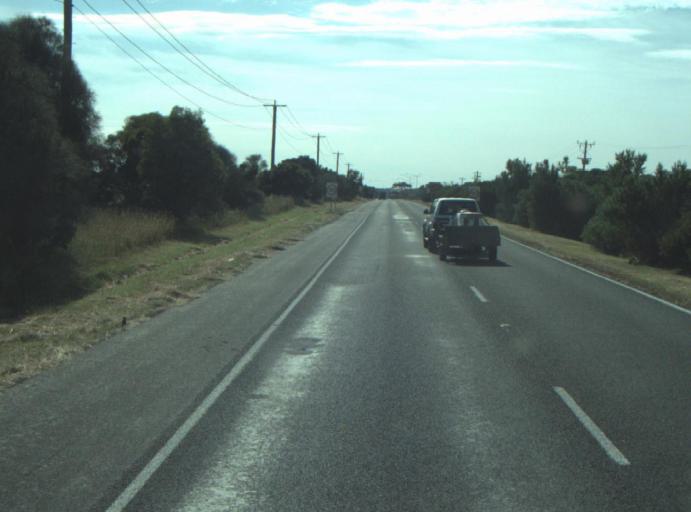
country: AU
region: Victoria
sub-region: Greater Geelong
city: Leopold
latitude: -38.1801
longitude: 144.5072
